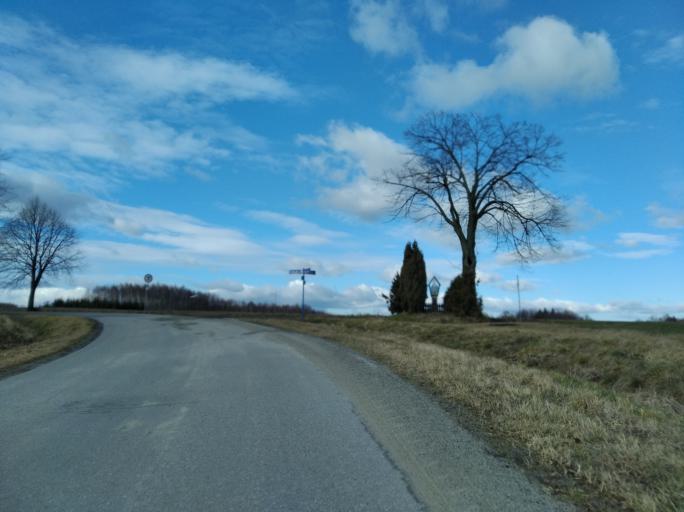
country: PL
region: Subcarpathian Voivodeship
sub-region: Powiat strzyzowski
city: Wisniowa
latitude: 49.9172
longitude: 21.6591
